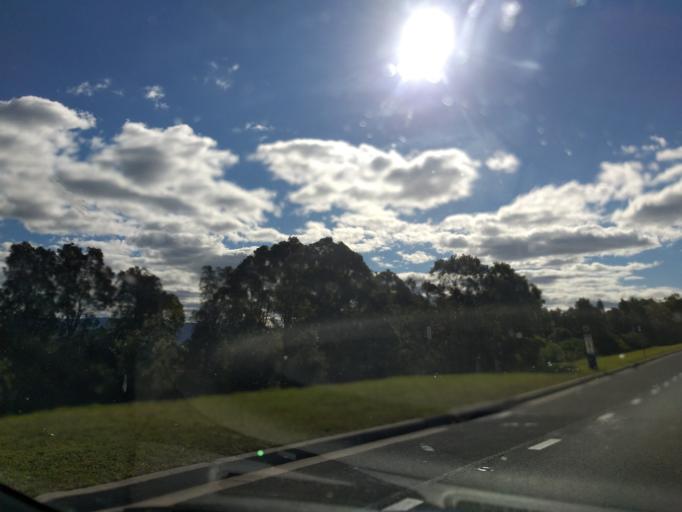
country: AU
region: New South Wales
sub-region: Shellharbour
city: Albion Park Rail
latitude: -34.5699
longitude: 150.8236
